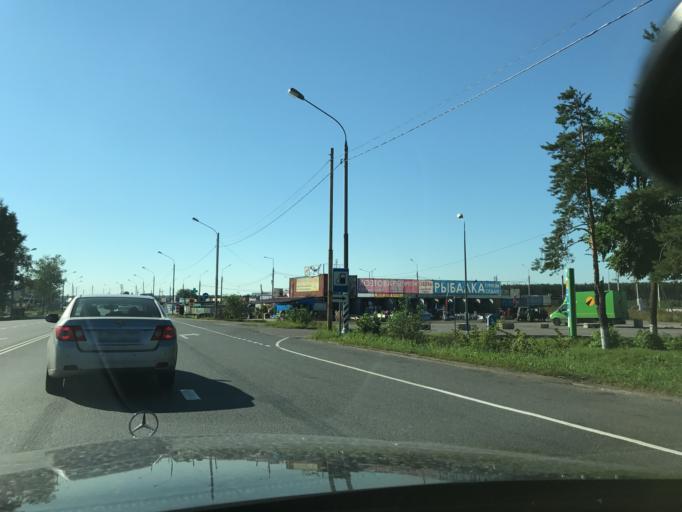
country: RU
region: Moskovskaya
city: Noginsk-9
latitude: 56.1116
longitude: 38.6166
